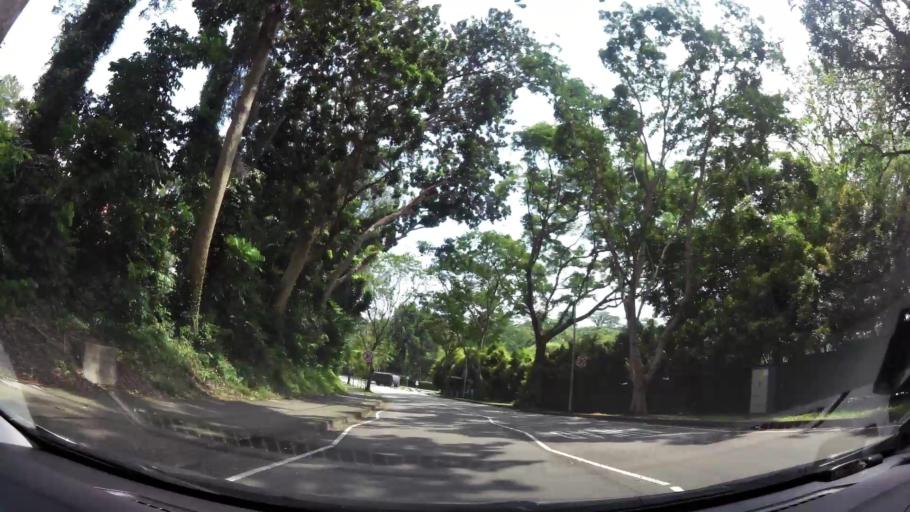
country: MY
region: Johor
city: Kampung Pasir Gudang Baru
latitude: 1.3880
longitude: 103.9778
